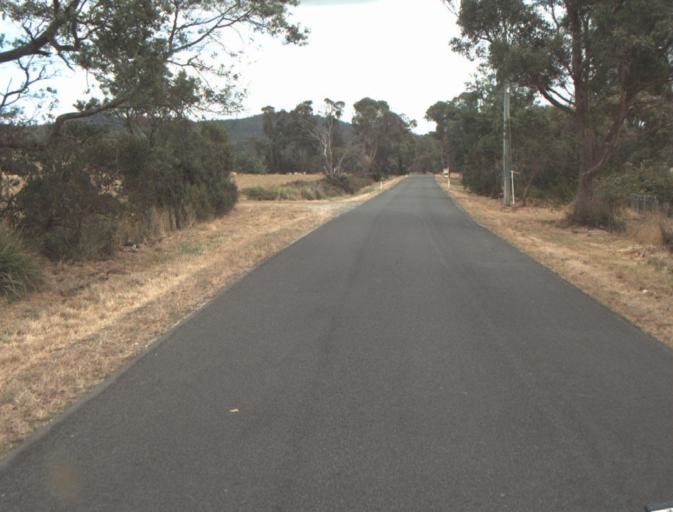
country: AU
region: Tasmania
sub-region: Launceston
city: Mayfield
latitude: -41.2093
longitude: 147.0591
